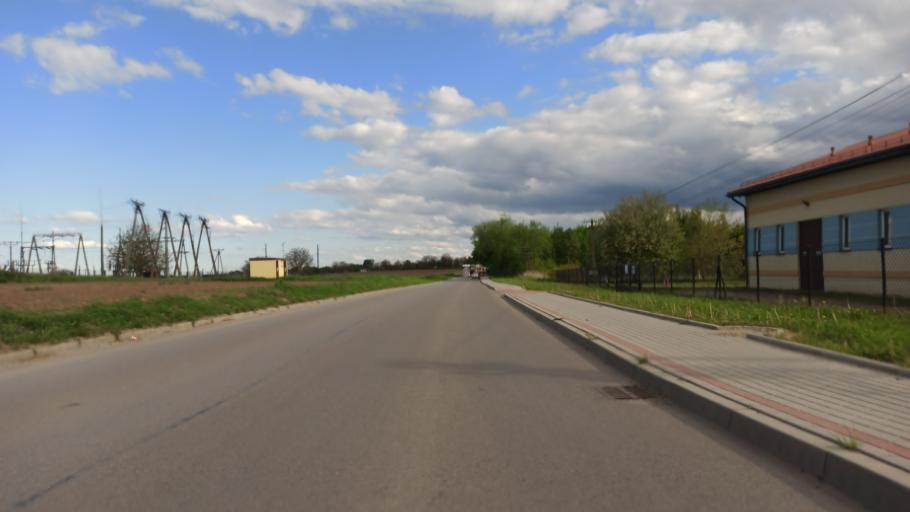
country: PL
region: Subcarpathian Voivodeship
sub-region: Powiat jaroslawski
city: Radymno
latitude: 49.9368
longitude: 22.8362
